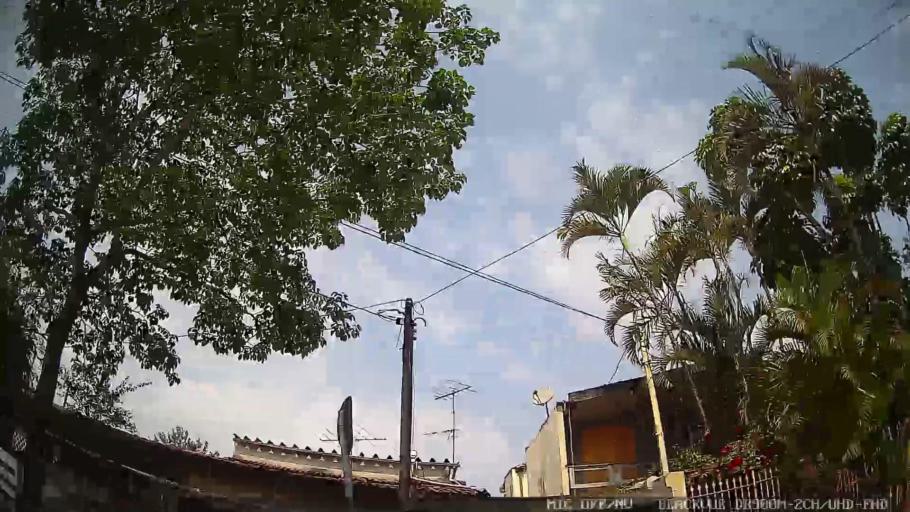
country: BR
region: Sao Paulo
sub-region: Taboao Da Serra
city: Taboao da Serra
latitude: -23.6472
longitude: -46.7226
